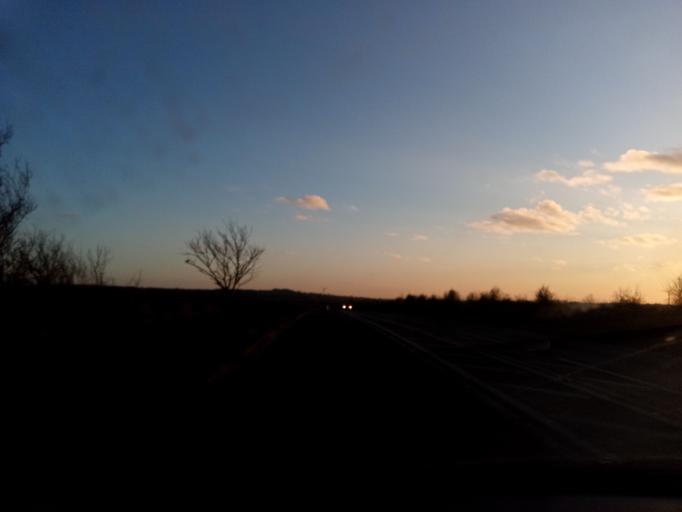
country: GB
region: England
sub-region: Nottinghamshire
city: Farnsfield
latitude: 53.1146
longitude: -1.0645
